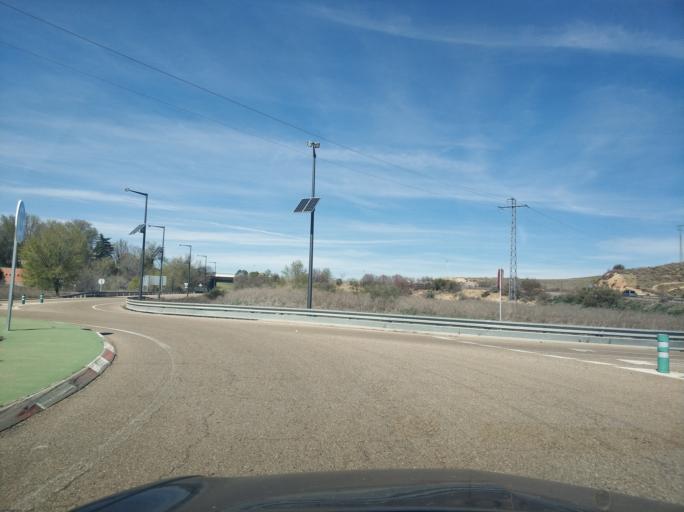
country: ES
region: Castille and Leon
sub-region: Provincia de Valladolid
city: Simancas
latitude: 41.5957
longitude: -4.8195
